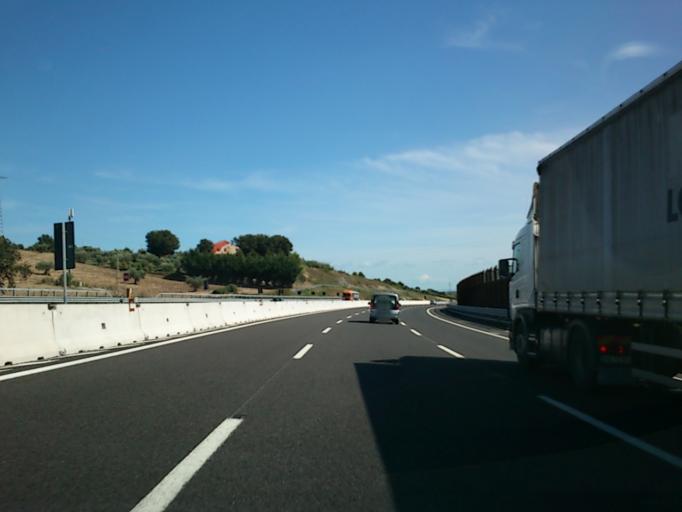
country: IT
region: The Marches
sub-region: Provincia di Pesaro e Urbino
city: Fenile
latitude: 43.8514
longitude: 12.9576
